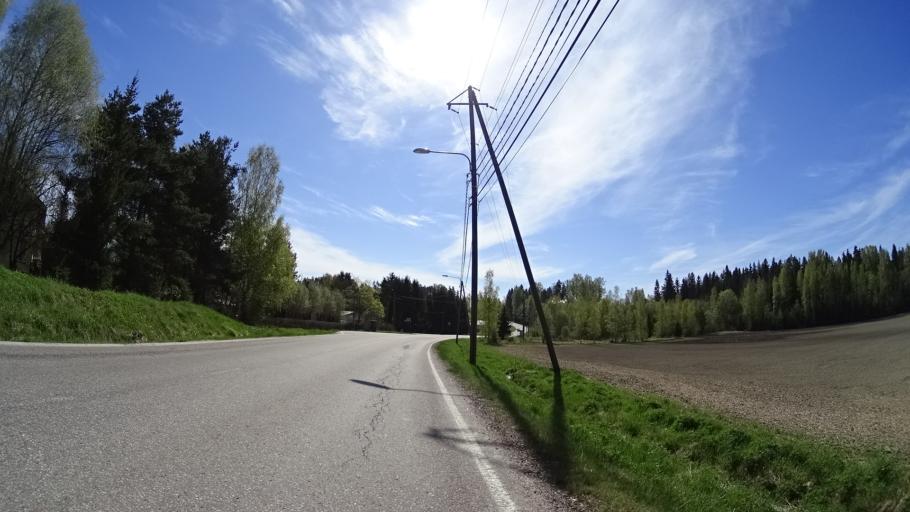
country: FI
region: Uusimaa
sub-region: Helsinki
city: Nurmijaervi
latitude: 60.3665
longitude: 24.8465
